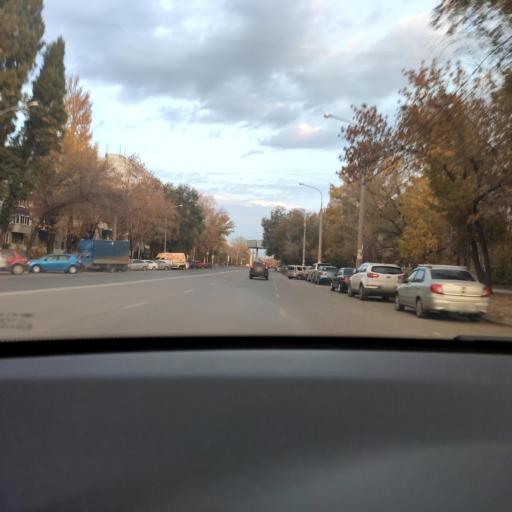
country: RU
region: Samara
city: Samara
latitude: 53.2269
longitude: 50.2096
